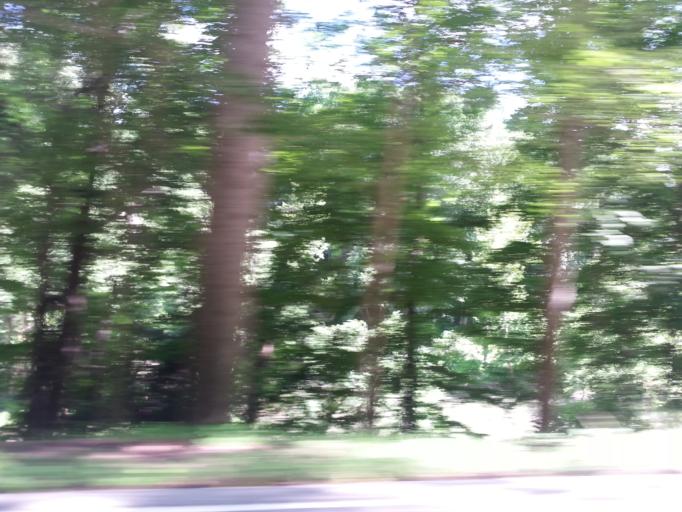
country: US
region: Kentucky
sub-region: Harlan County
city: Cumberland
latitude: 36.9298
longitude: -83.1600
